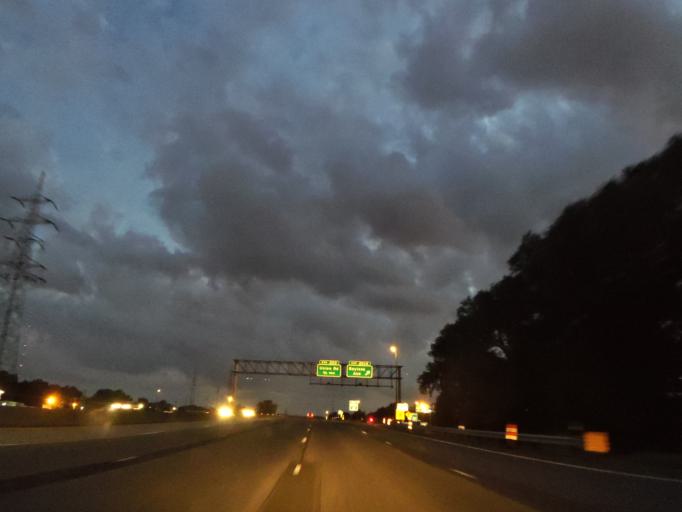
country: US
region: Missouri
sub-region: Saint Louis County
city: Lemay
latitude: 38.5484
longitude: -90.2878
